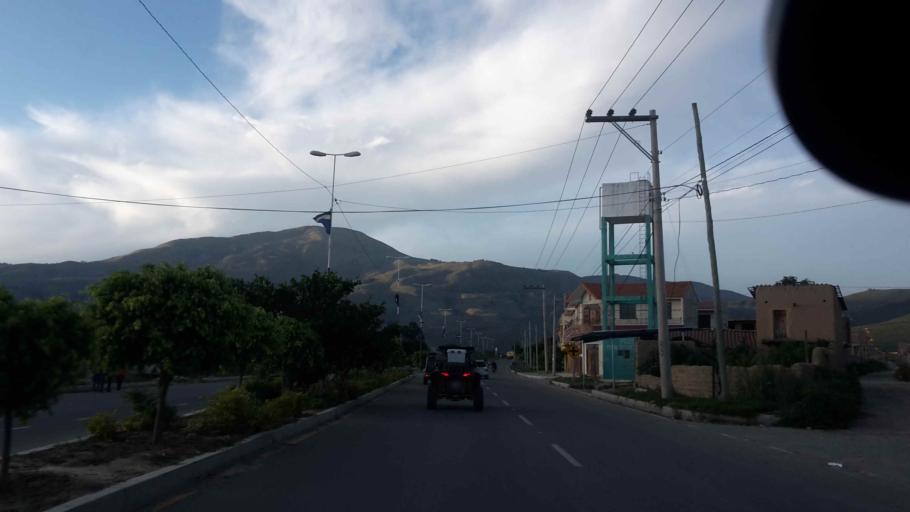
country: BO
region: Cochabamba
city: Punata
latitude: -17.5374
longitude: -65.8359
